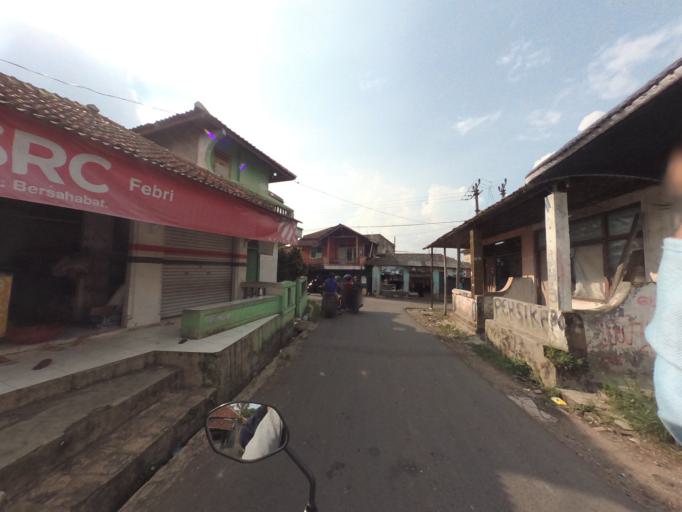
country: ID
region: West Java
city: Ciampea
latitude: -6.6056
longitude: 106.7059
